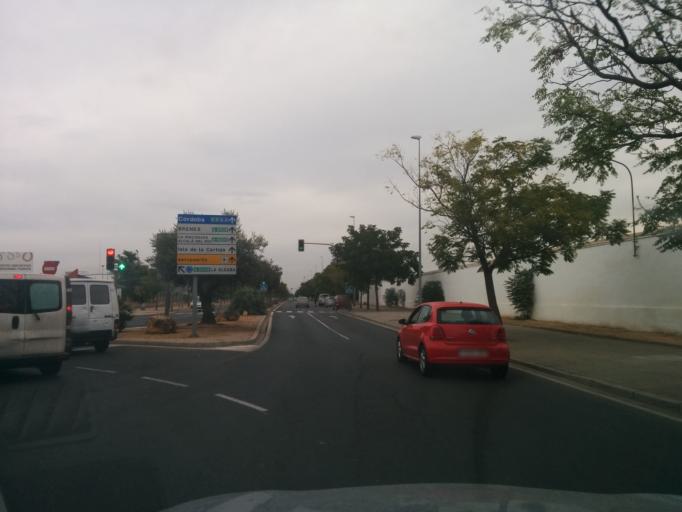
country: ES
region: Andalusia
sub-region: Provincia de Sevilla
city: Sevilla
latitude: 37.4218
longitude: -5.9825
